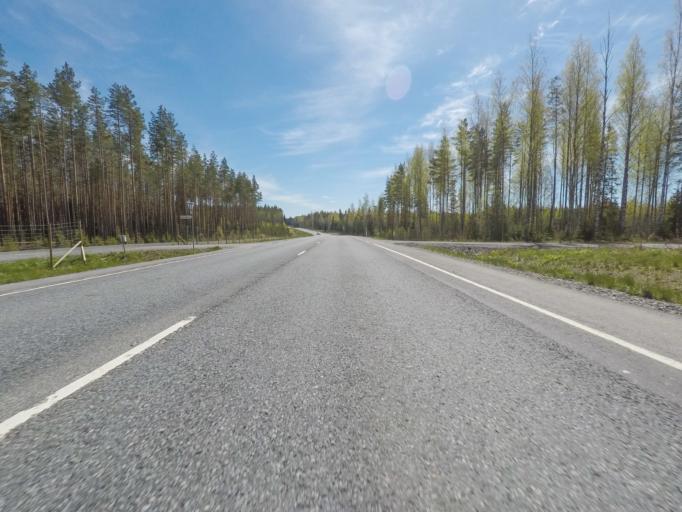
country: FI
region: Haeme
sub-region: Forssa
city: Tammela
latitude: 60.7185
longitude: 23.7538
